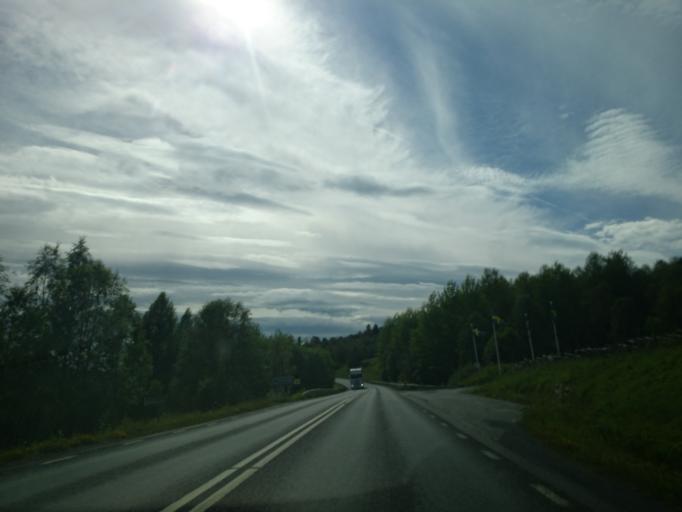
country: SE
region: Jaemtland
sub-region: Are Kommun
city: Jarpen
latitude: 63.3209
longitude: 13.3602
